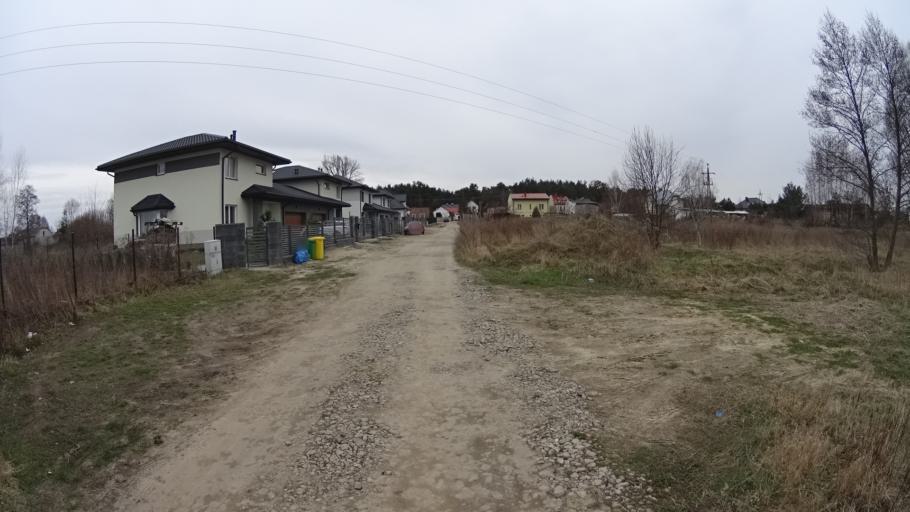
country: PL
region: Masovian Voivodeship
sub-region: Powiat warszawski zachodni
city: Hornowek
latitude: 52.2654
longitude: 20.7856
